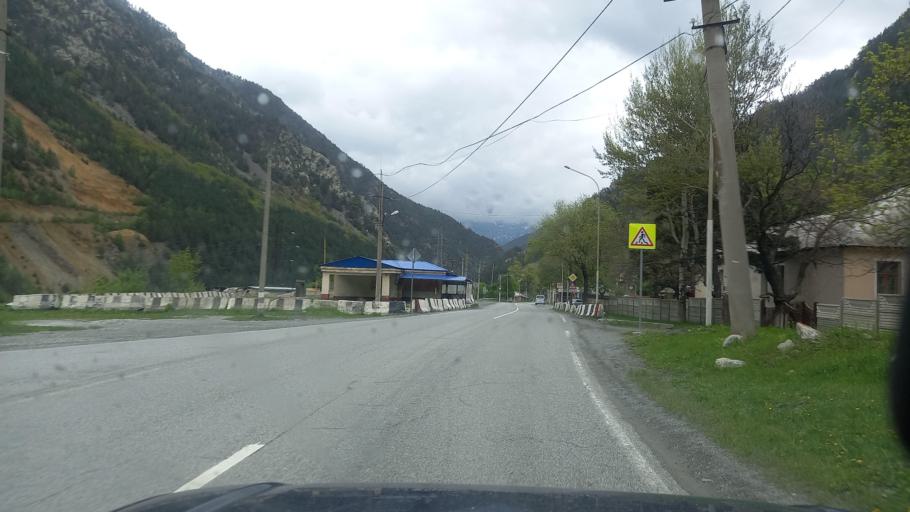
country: RU
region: North Ossetia
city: Mizur
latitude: 42.7943
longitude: 44.0062
